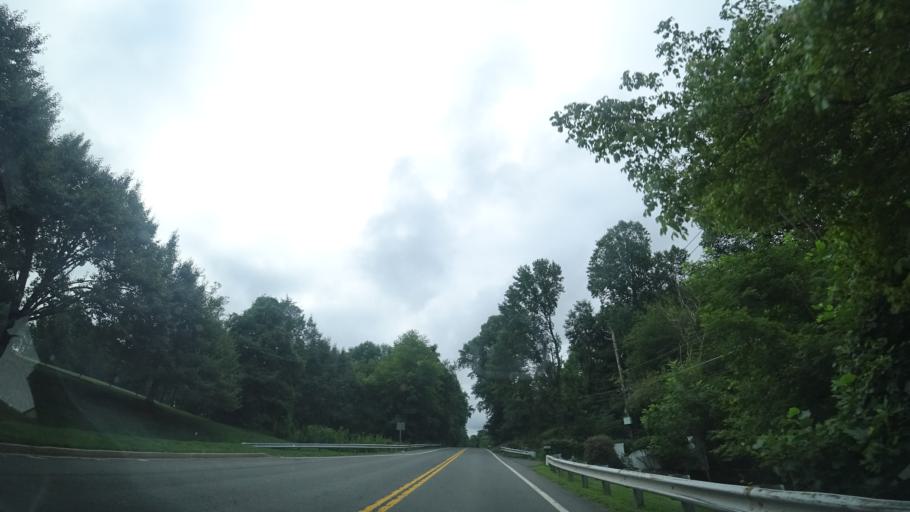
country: US
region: Virginia
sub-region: Loudoun County
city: Lowes Island
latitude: 39.0725
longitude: -77.3212
